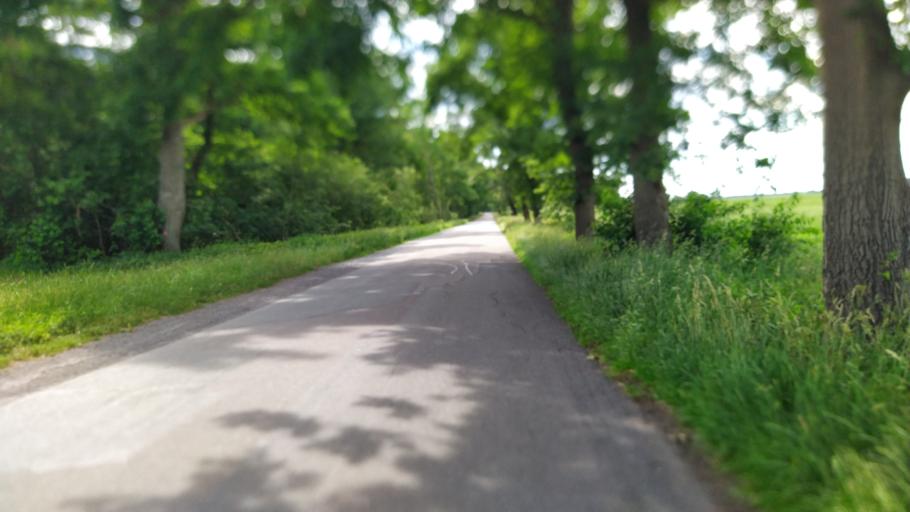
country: DE
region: Lower Saxony
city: Armstorf
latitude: 53.6068
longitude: 9.0493
